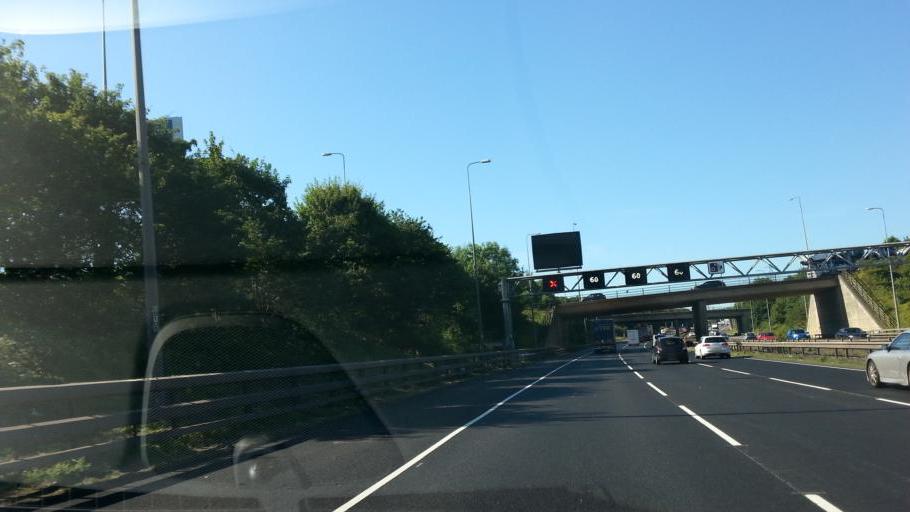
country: GB
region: England
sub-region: Solihull
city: Bickenhill
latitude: 52.4473
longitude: -1.7089
